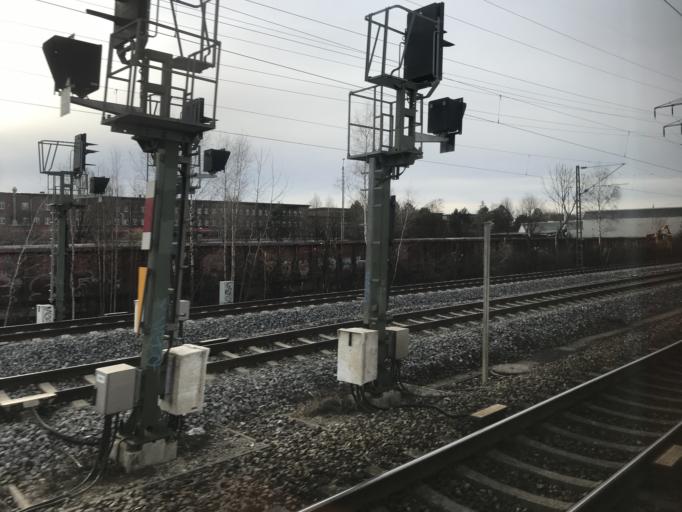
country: DE
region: Bavaria
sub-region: Upper Bavaria
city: Pasing
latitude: 48.1652
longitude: 11.4287
